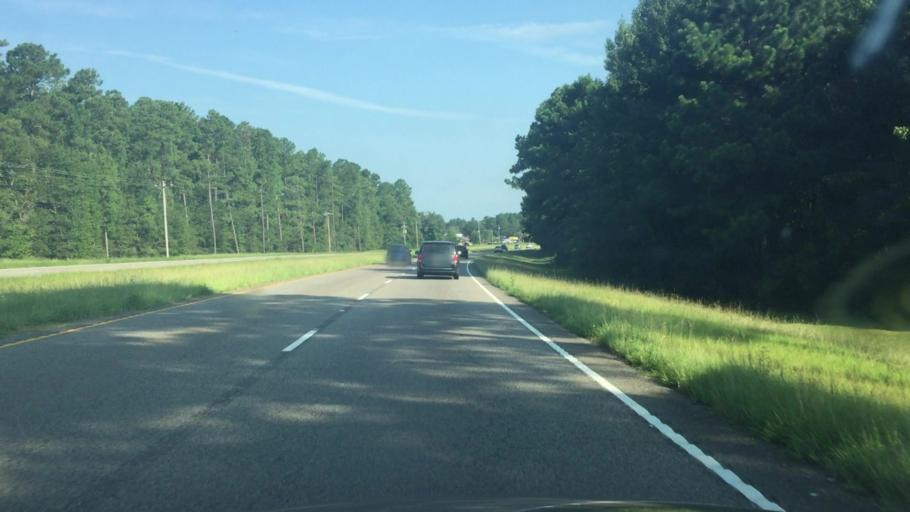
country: US
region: South Carolina
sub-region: Horry County
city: North Myrtle Beach
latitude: 33.9195
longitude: -78.7239
